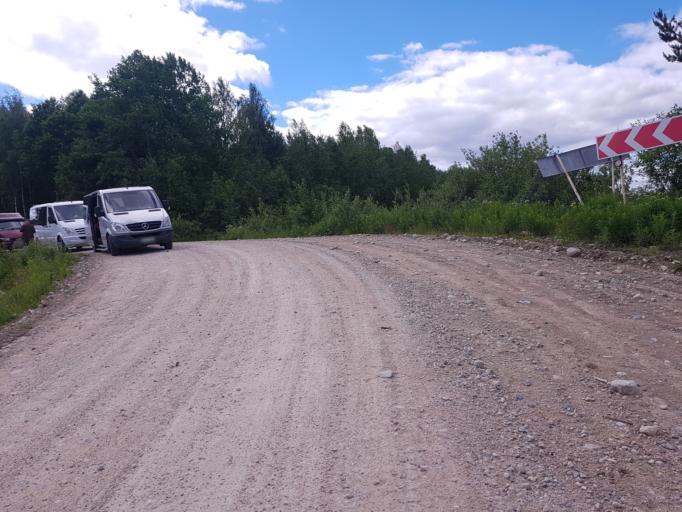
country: RU
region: Republic of Karelia
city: Kostomuksha
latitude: 65.1683
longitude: 30.2965
